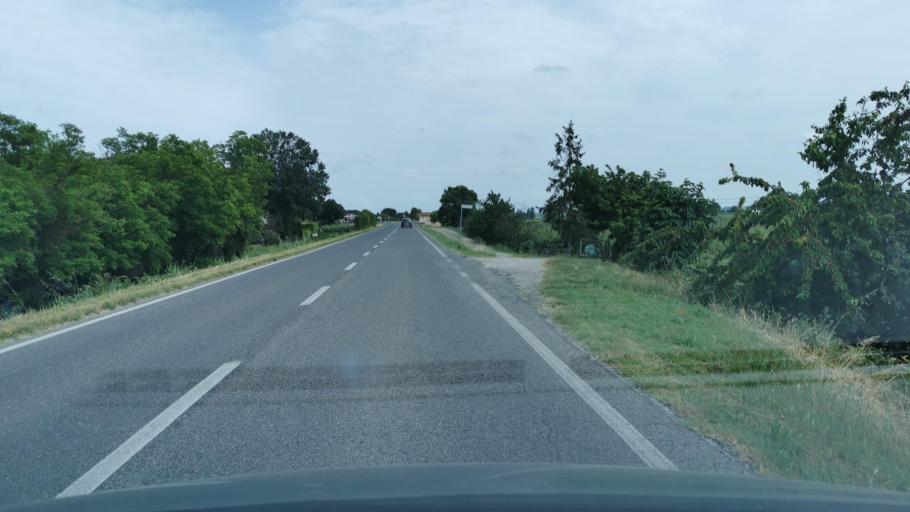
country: IT
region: Emilia-Romagna
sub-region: Provincia di Ravenna
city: Sant'Alberto
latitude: 44.5390
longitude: 12.1511
